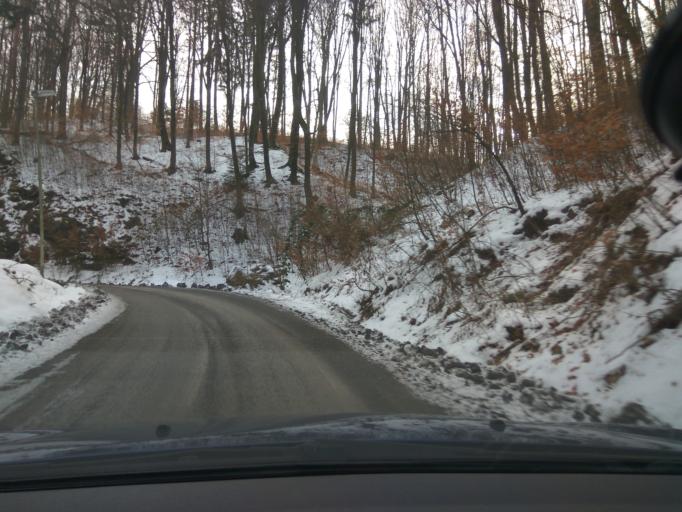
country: SK
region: Banskobystricky
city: Zarnovica
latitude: 48.4807
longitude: 18.7491
